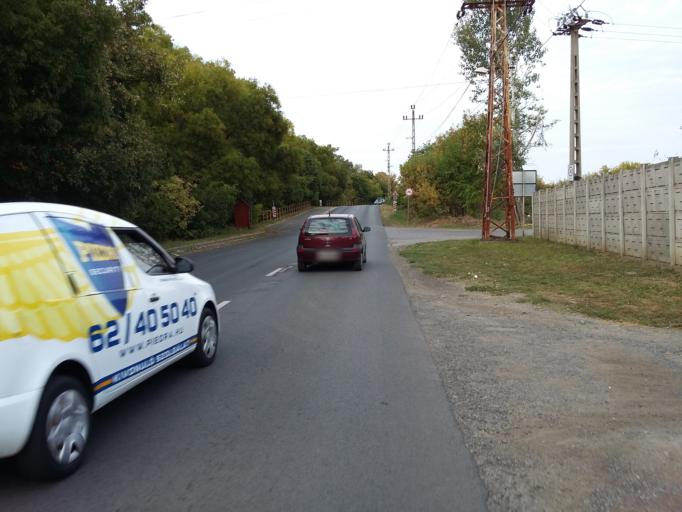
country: HU
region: Csongrad
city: Szeged
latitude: 46.2312
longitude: 20.1184
